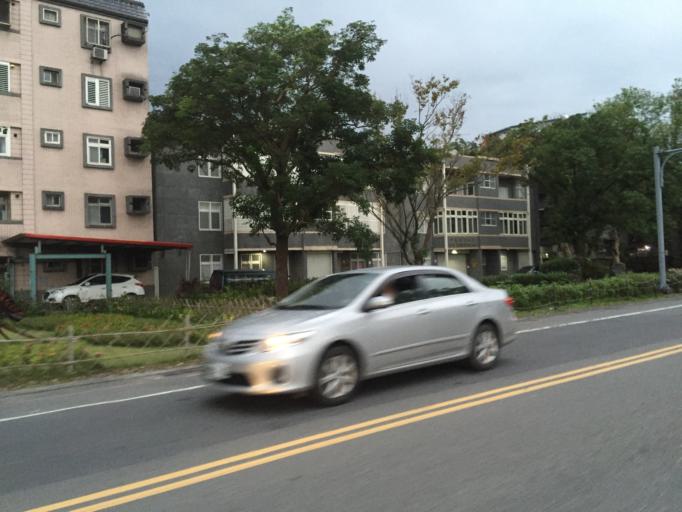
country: TW
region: Taiwan
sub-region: Yilan
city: Yilan
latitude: 24.7543
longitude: 121.7487
